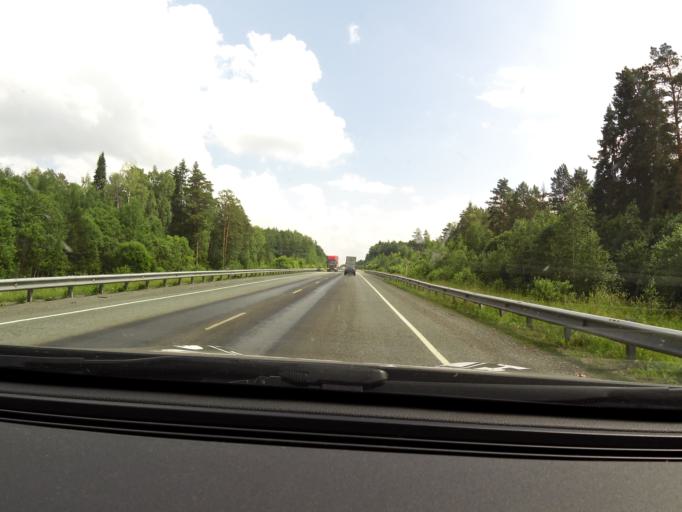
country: RU
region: Sverdlovsk
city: Achit
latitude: 56.8394
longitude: 57.7564
